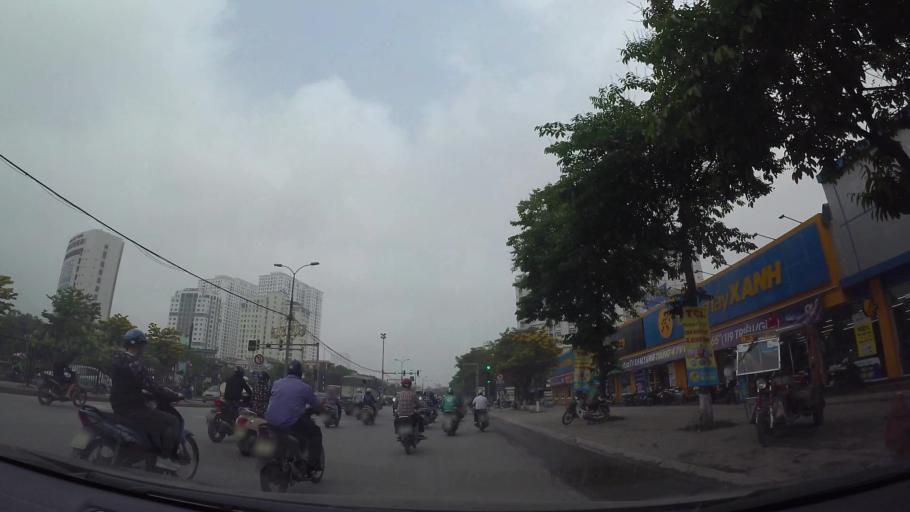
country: VN
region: Ha Noi
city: Van Dien
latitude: 20.9699
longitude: 105.8416
